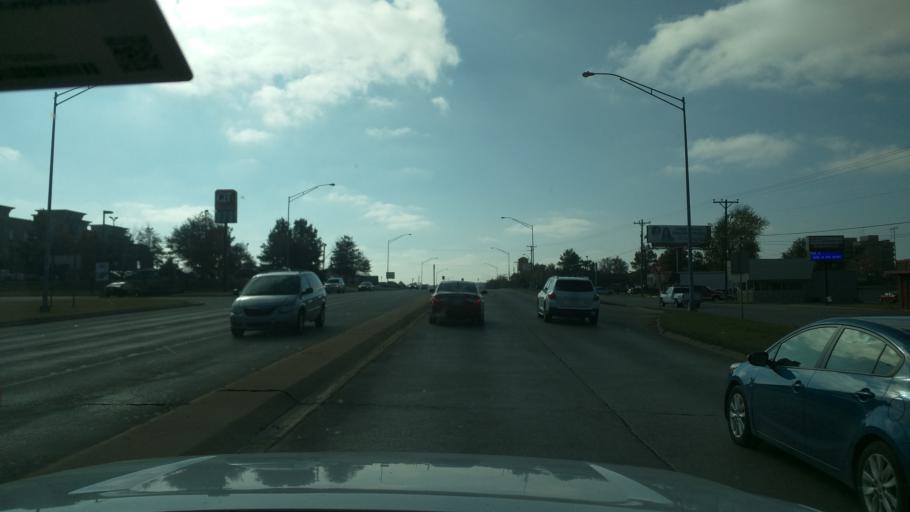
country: US
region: Oklahoma
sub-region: Washington County
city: Dewey
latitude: 36.7569
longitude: -95.9356
